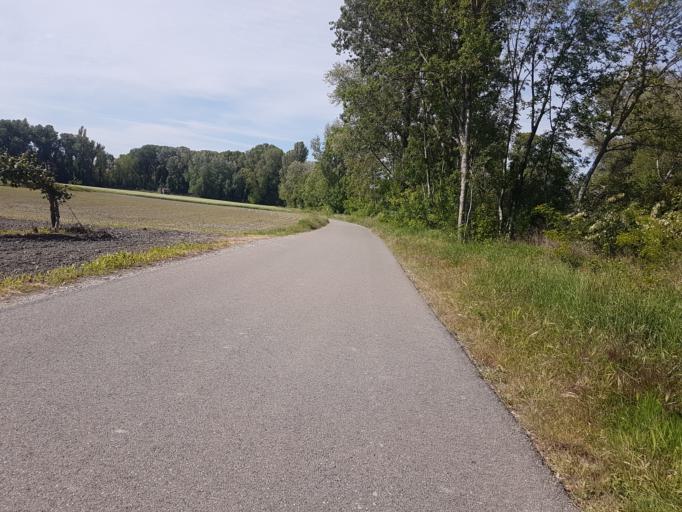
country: FR
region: Rhone-Alpes
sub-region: Departement de l'Ardeche
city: La Voulte-sur-Rhone
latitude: 44.7865
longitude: 4.7759
